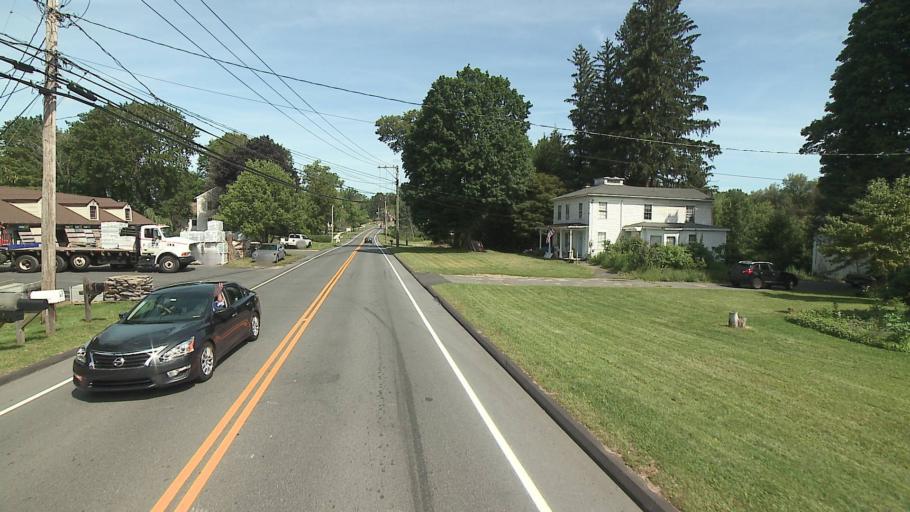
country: US
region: Connecticut
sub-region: Litchfield County
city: Bethlehem Village
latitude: 41.6356
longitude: -73.2088
